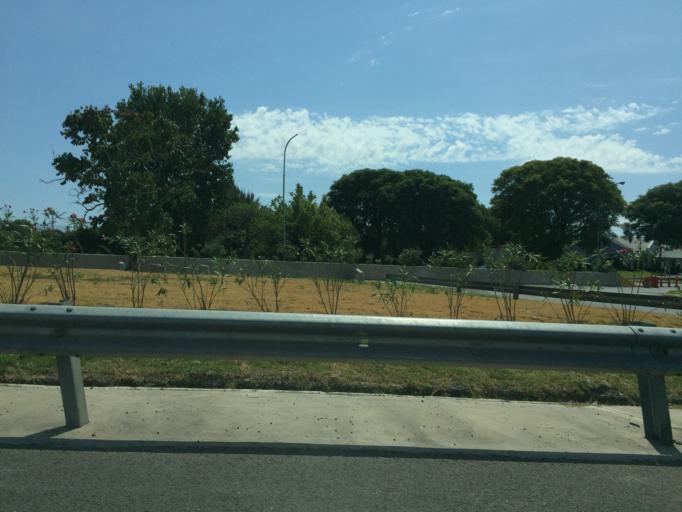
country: AR
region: Buenos Aires F.D.
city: Colegiales
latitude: -34.5511
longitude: -58.4328
